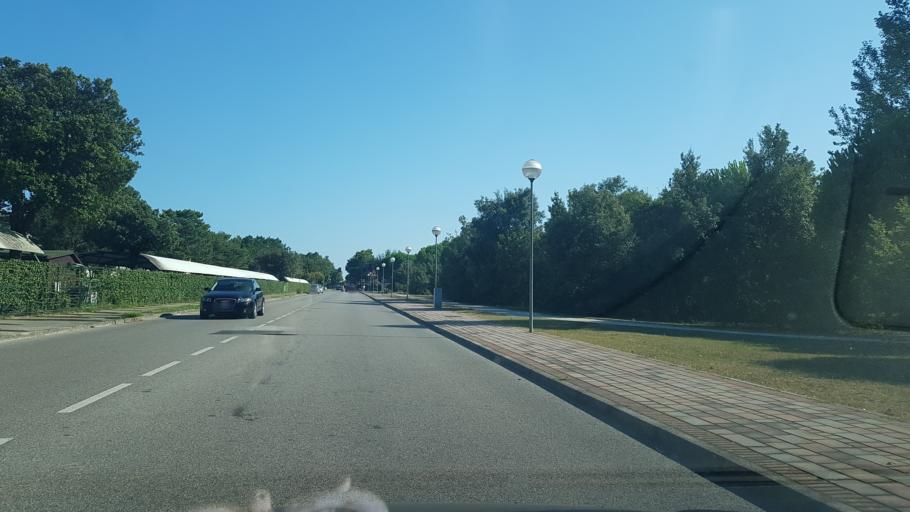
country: IT
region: Veneto
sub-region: Provincia di Venezia
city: Bibione
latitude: 45.6397
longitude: 13.0398
